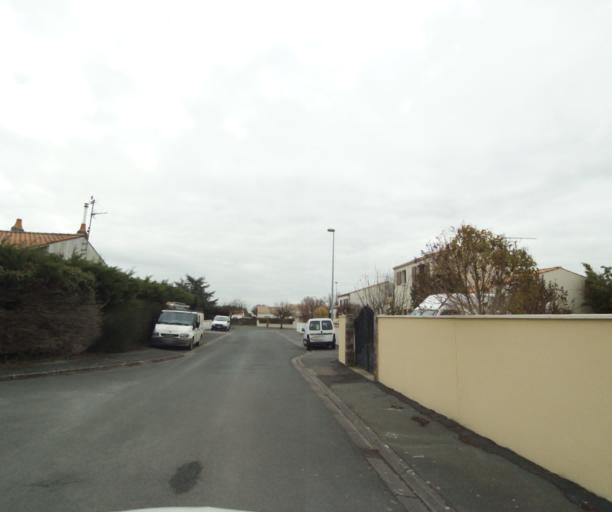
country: FR
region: Poitou-Charentes
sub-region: Departement de la Charente-Maritime
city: Lagord
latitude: 46.1893
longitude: -1.1510
